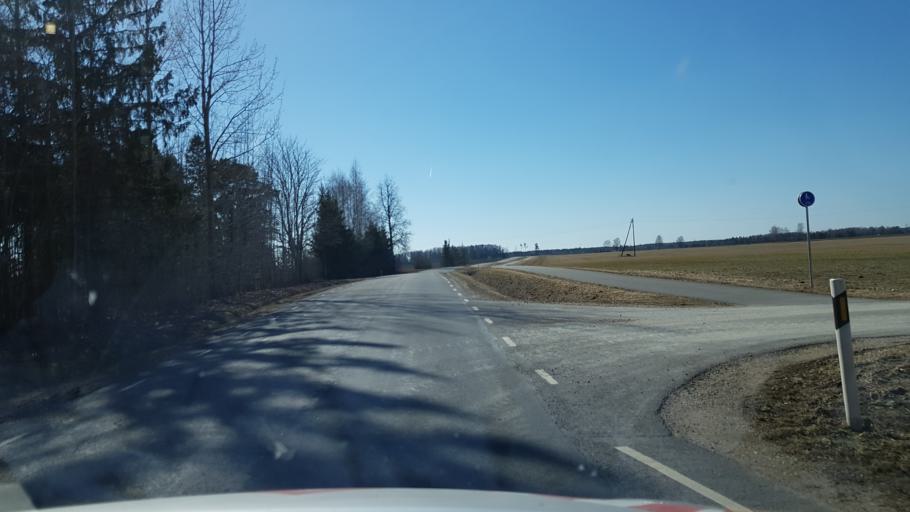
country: EE
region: Laeaene-Virumaa
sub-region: Vaeike-Maarja vald
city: Vaike-Maarja
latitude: 59.0941
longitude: 26.2084
